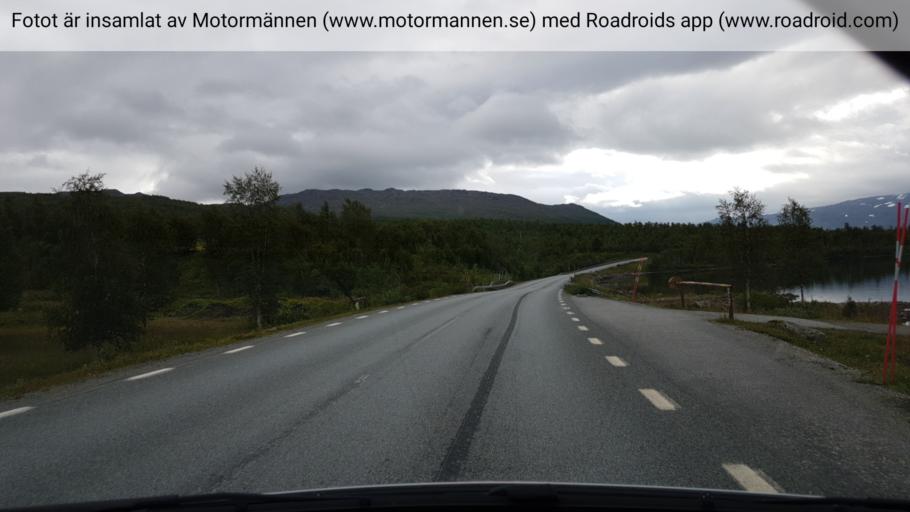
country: NO
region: Nordland
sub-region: Rana
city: Mo i Rana
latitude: 66.1017
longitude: 14.8456
